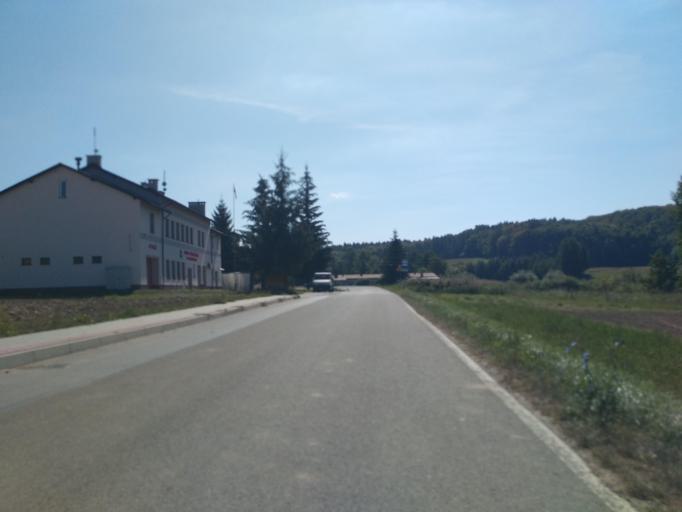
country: PL
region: Subcarpathian Voivodeship
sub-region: Powiat brzozowski
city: Niebocko
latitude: 49.6551
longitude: 22.1378
